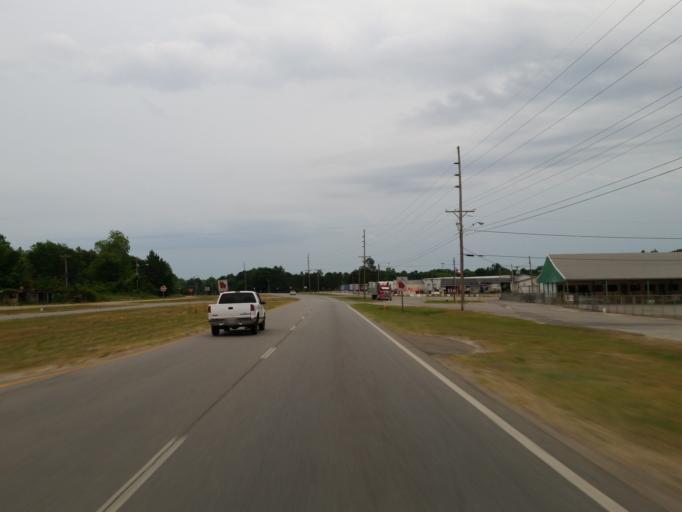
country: US
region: Georgia
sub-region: Crisp County
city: Cordele
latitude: 31.9894
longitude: -83.7933
